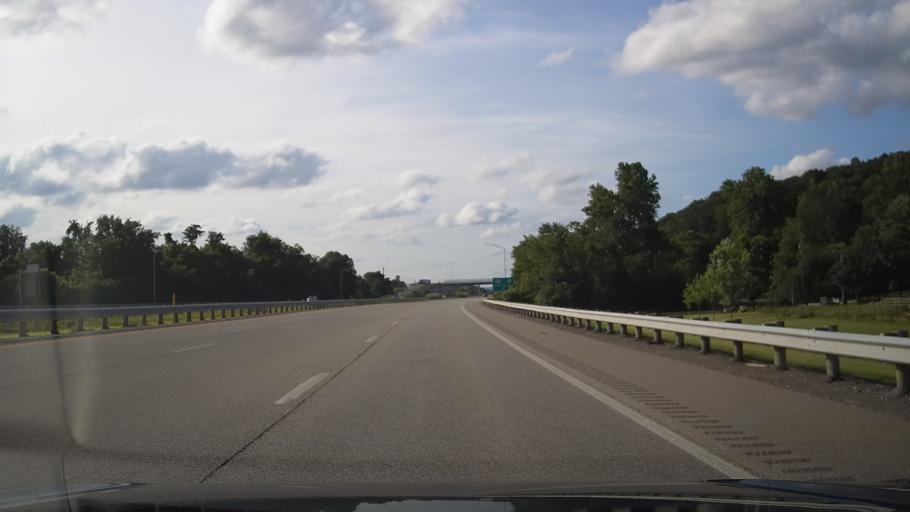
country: US
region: Ohio
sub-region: Scioto County
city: Franklin Furnace
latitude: 38.6424
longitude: -82.8489
